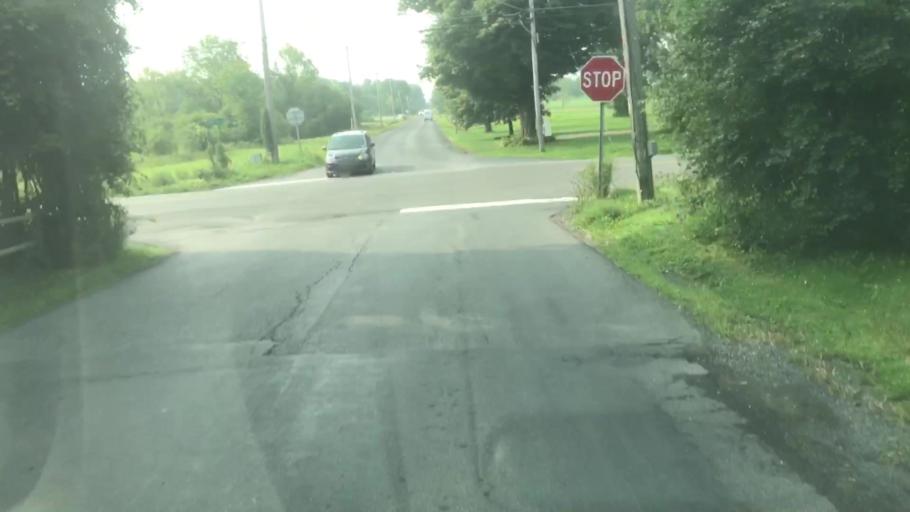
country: US
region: New York
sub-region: Onondaga County
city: Skaneateles
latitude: 42.9436
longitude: -76.4585
